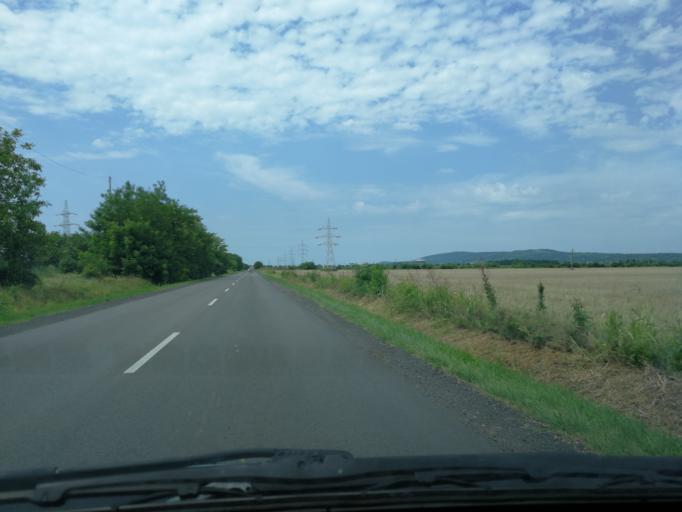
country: HU
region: Baranya
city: Siklos
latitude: 45.8485
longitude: 18.3762
